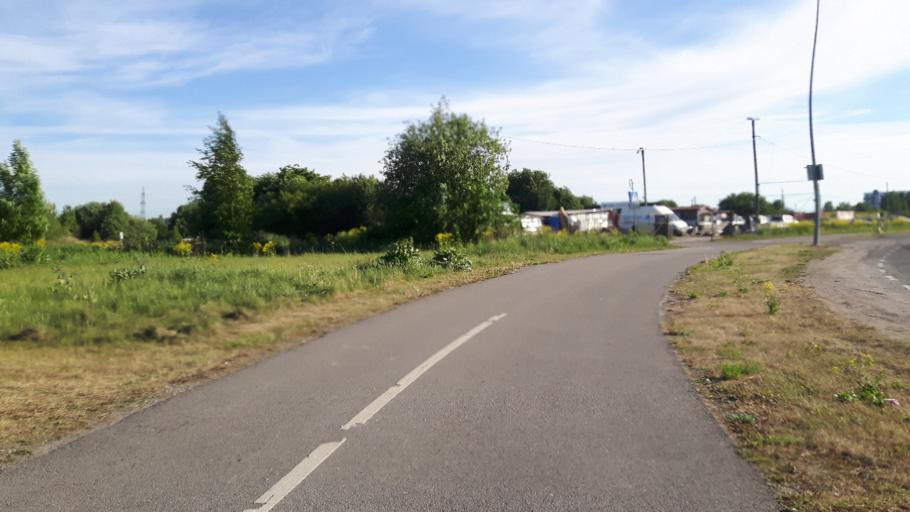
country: EE
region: Harju
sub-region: Tallinna linn
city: Kose
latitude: 59.4496
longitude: 24.8330
